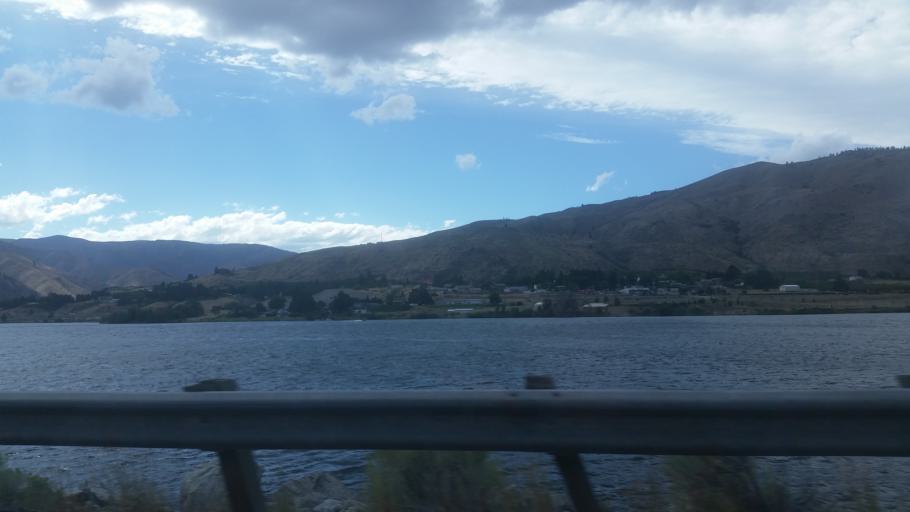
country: US
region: Washington
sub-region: Chelan County
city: Entiat
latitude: 47.6743
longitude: -120.1989
